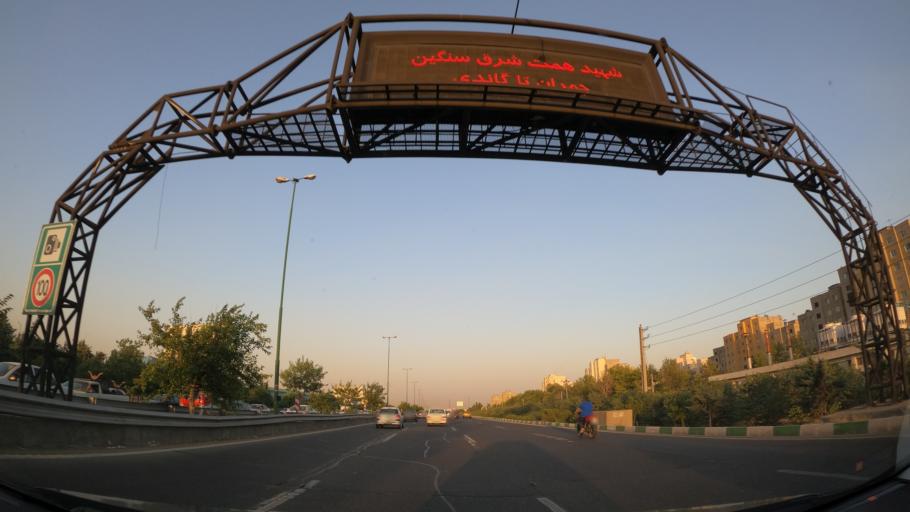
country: IR
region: Tehran
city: Tehran
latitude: 35.7152
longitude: 51.3215
